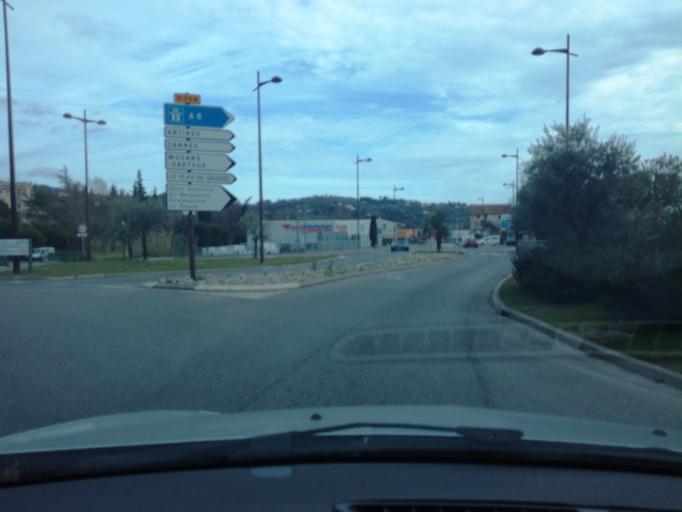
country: FR
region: Provence-Alpes-Cote d'Azur
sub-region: Departement des Alpes-Maritimes
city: Grasse
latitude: 43.6536
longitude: 6.9442
